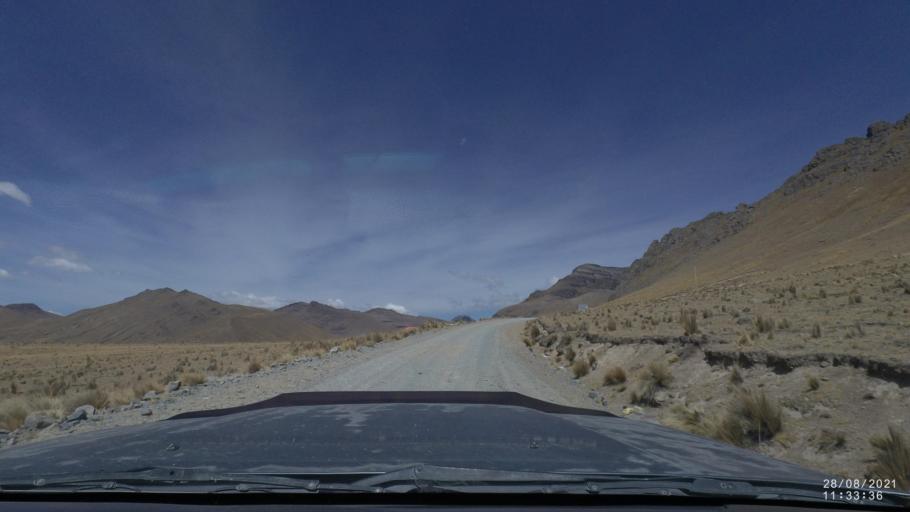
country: BO
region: Cochabamba
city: Sipe Sipe
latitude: -17.1866
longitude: -66.3710
